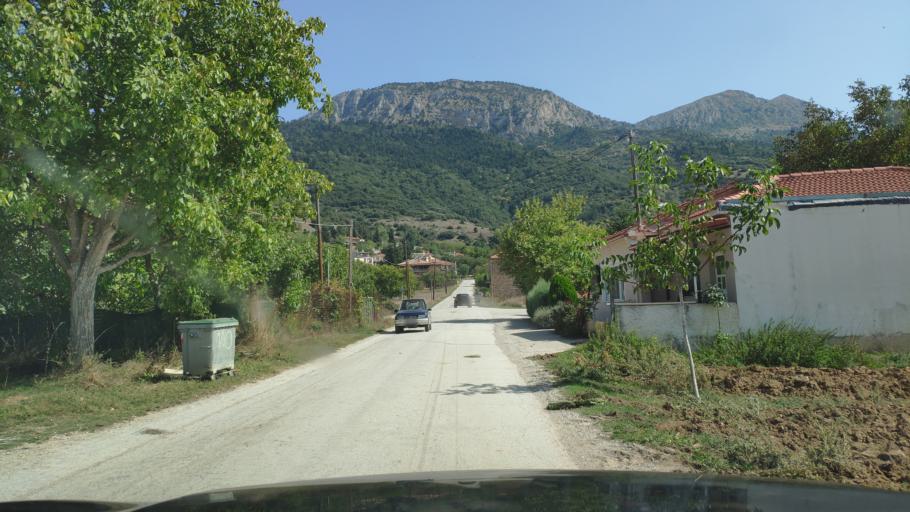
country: GR
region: West Greece
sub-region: Nomos Achaias
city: Aiyira
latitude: 37.9085
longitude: 22.3280
